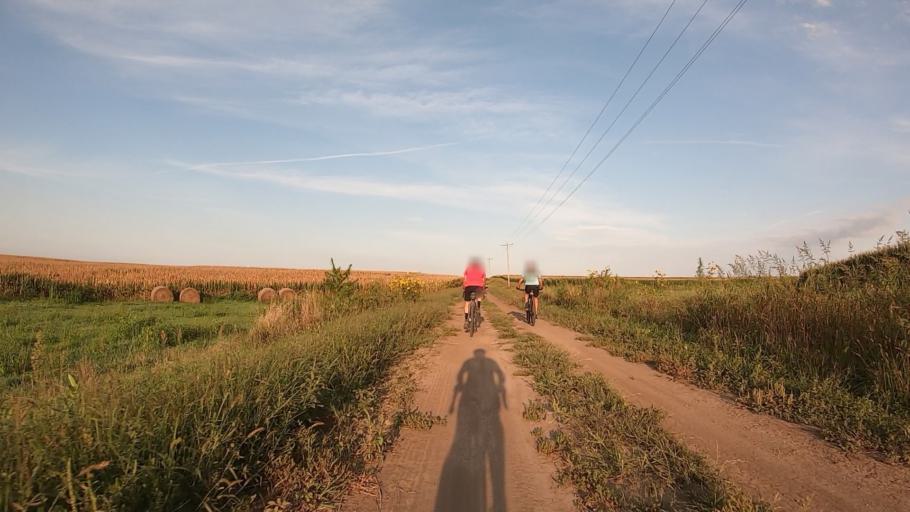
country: US
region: Kansas
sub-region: Marshall County
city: Marysville
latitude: 39.7693
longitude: -96.7236
